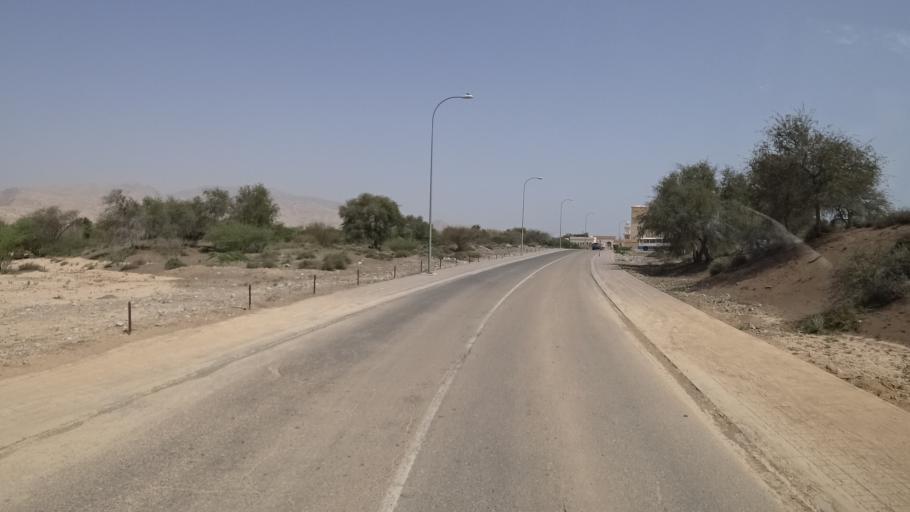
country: OM
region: Muhafazat Masqat
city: Muscat
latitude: 23.2360
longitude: 58.9101
